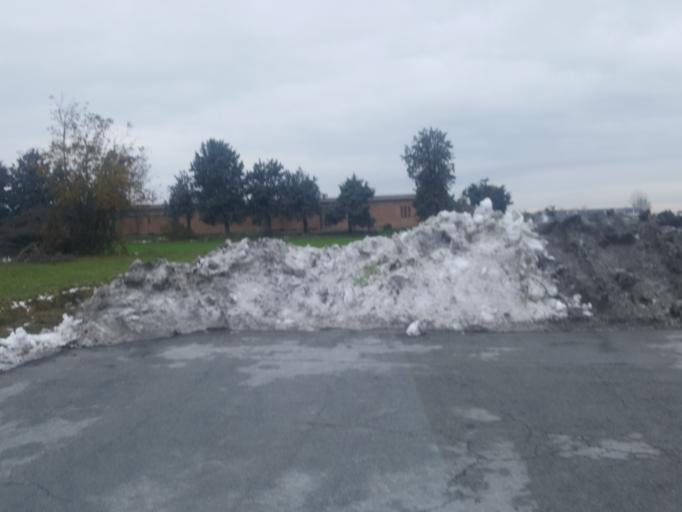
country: IT
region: Piedmont
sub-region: Provincia di Cuneo
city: Breo
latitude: 44.4014
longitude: 7.8234
